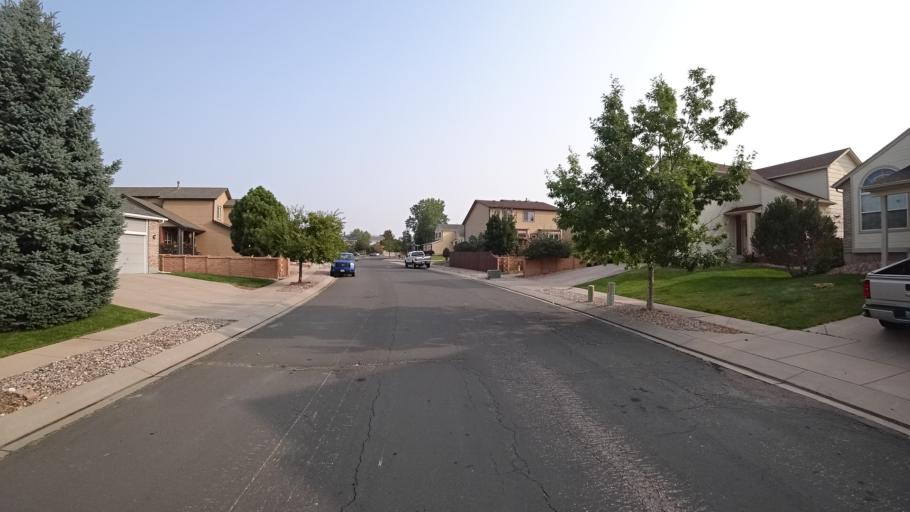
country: US
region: Colorado
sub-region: El Paso County
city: Black Forest
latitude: 38.9357
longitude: -104.7266
